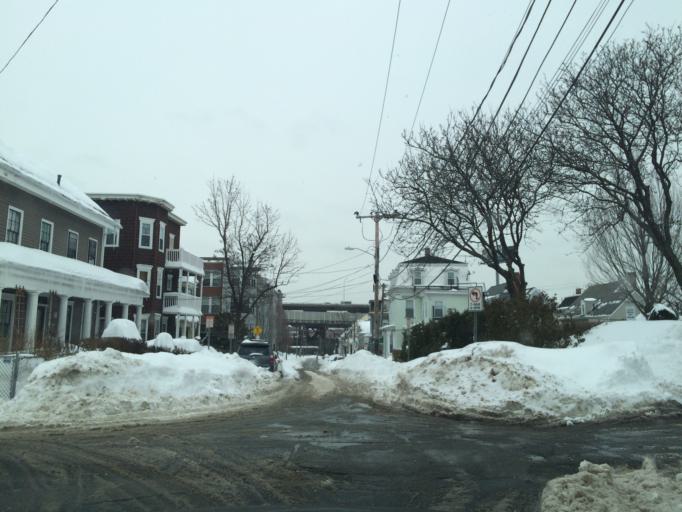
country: US
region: Massachusetts
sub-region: Middlesex County
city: Somerville
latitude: 42.3845
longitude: -71.0793
